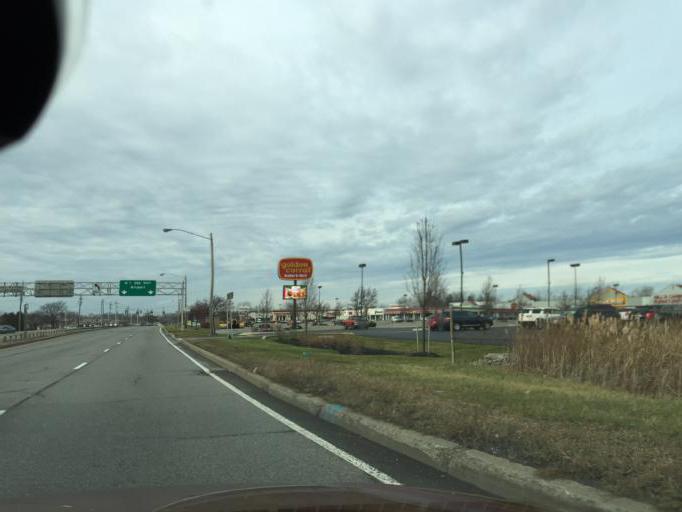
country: US
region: New York
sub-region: Monroe County
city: Rochester
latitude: 43.0890
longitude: -77.6396
